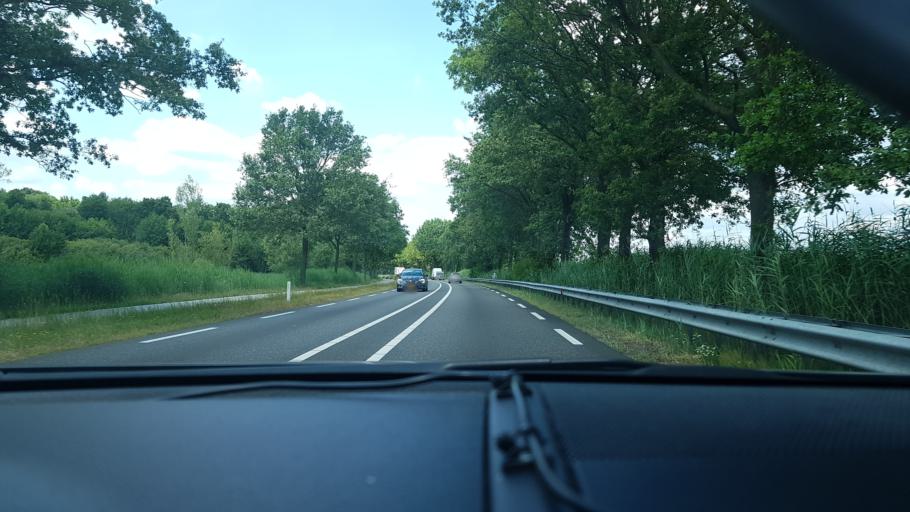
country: NL
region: North Brabant
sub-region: Gemeente Helmond
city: Helmond
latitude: 51.4401
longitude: 5.6924
